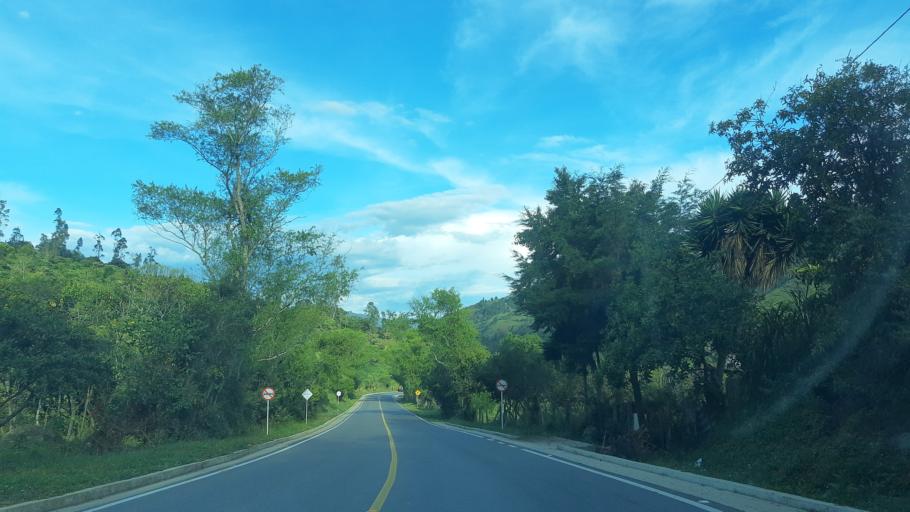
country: CO
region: Cundinamarca
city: Macheta
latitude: 5.0733
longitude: -73.6007
